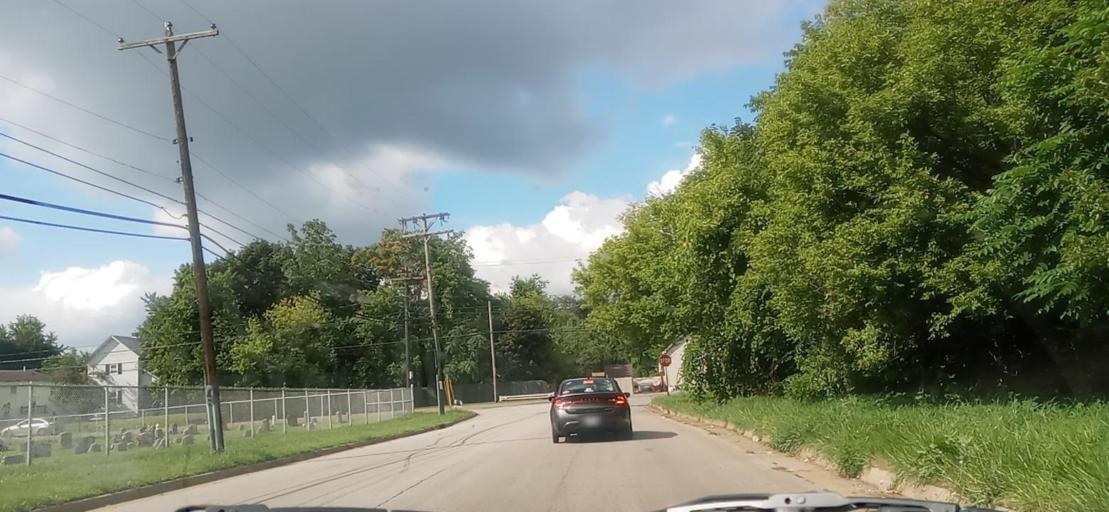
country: US
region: Ohio
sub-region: Summit County
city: Portage Lakes
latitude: 41.0318
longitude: -81.5632
